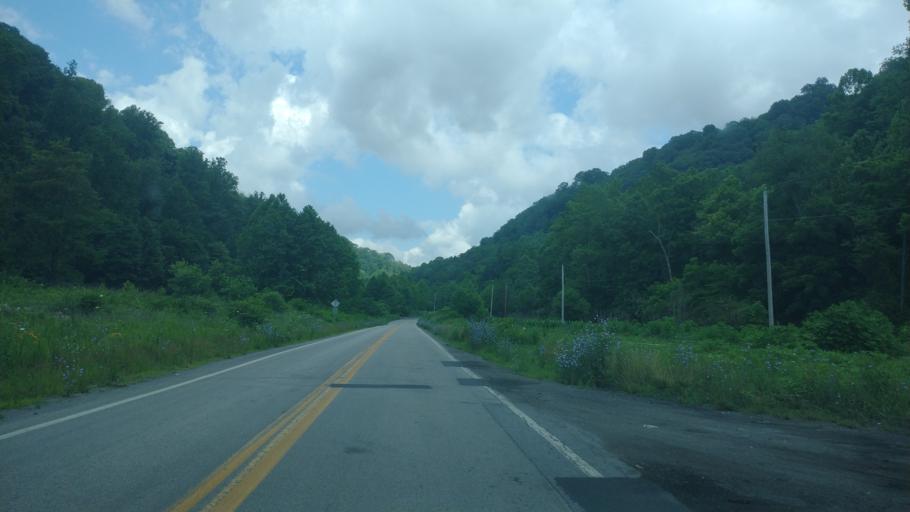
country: US
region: West Virginia
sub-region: McDowell County
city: Welch
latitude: 37.4121
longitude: -81.4740
